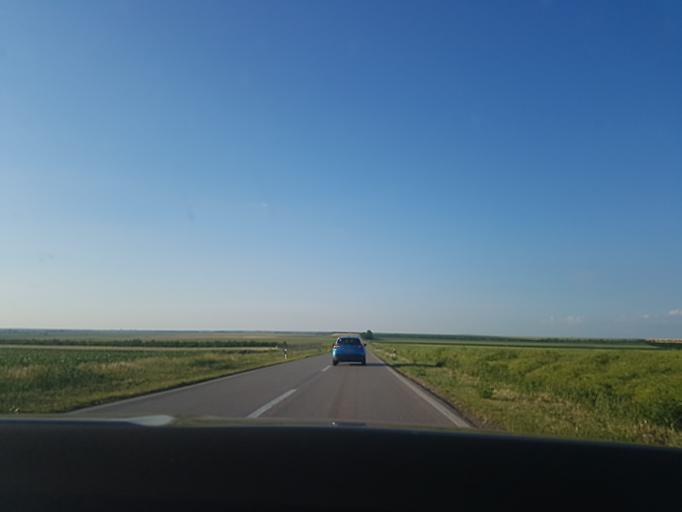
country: RS
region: Autonomna Pokrajina Vojvodina
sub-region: Juznobanatski Okrug
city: Vrsac
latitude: 45.1674
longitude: 21.2925
